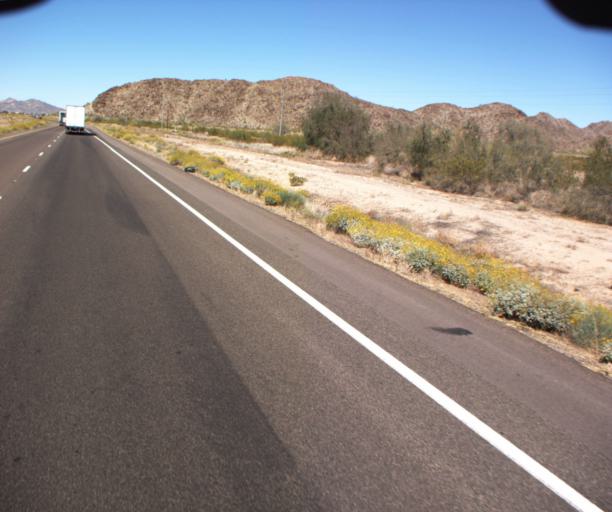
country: US
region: Arizona
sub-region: Maricopa County
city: Buckeye
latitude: 33.1649
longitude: -112.6498
